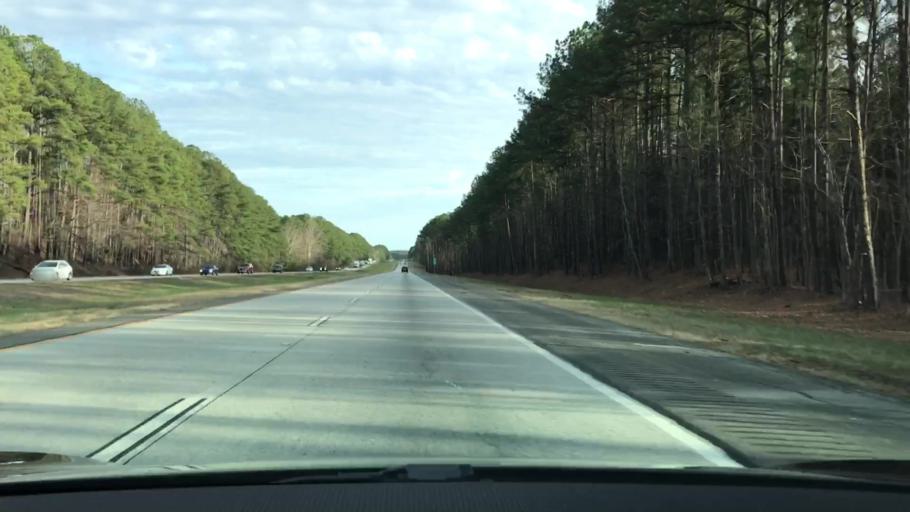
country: US
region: Georgia
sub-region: Taliaferro County
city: Crawfordville
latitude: 33.5097
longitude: -82.8428
